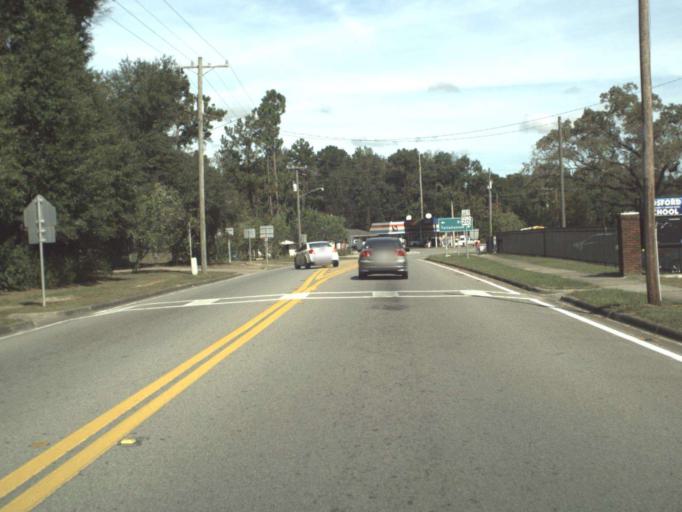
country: US
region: Florida
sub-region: Liberty County
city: Bristol
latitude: 30.3885
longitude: -84.7984
